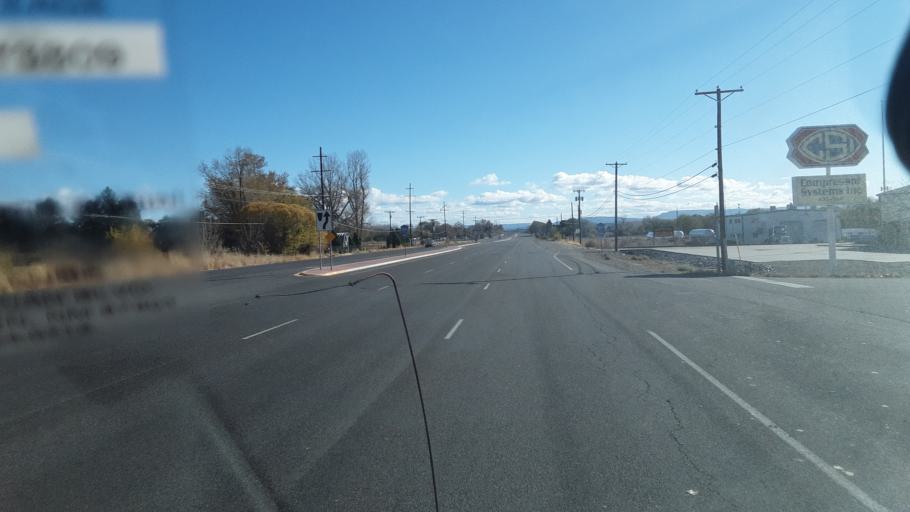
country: US
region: New Mexico
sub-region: San Juan County
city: Lee Acres
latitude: 36.7010
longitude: -108.0537
